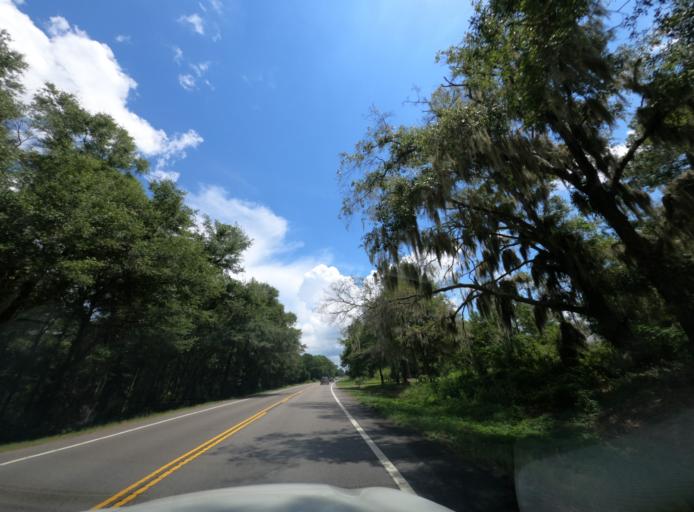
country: US
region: South Carolina
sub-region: Beaufort County
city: Beaufort
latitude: 32.3959
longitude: -80.5273
